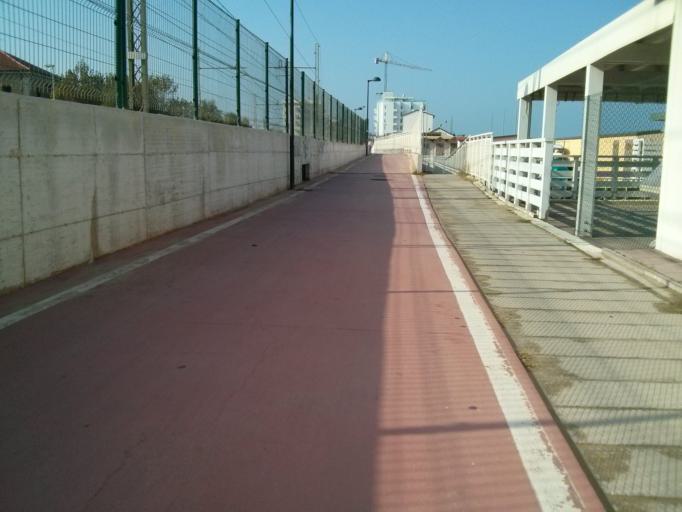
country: IT
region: The Marches
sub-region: Provincia di Pesaro e Urbino
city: Pesaro
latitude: 43.9053
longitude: 12.9303
